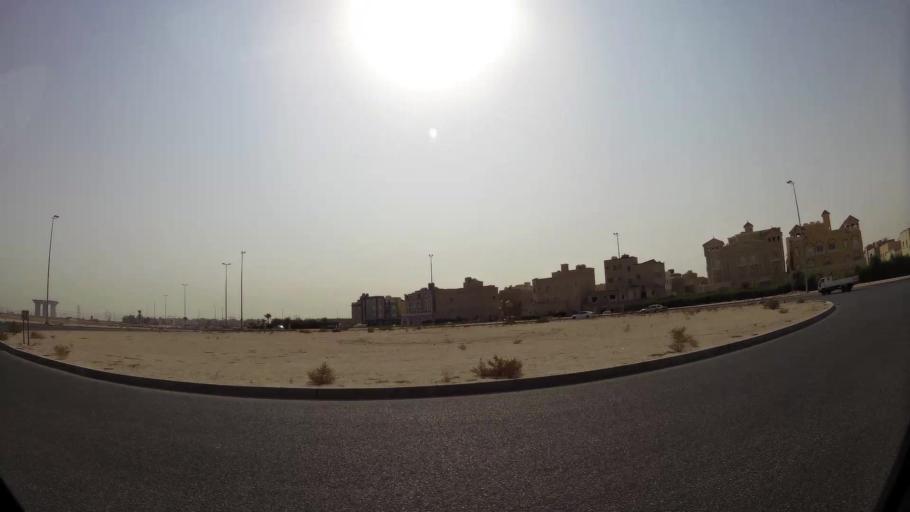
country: KW
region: Muhafazat al Jahra'
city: Al Jahra'
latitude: 29.3418
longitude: 47.7743
